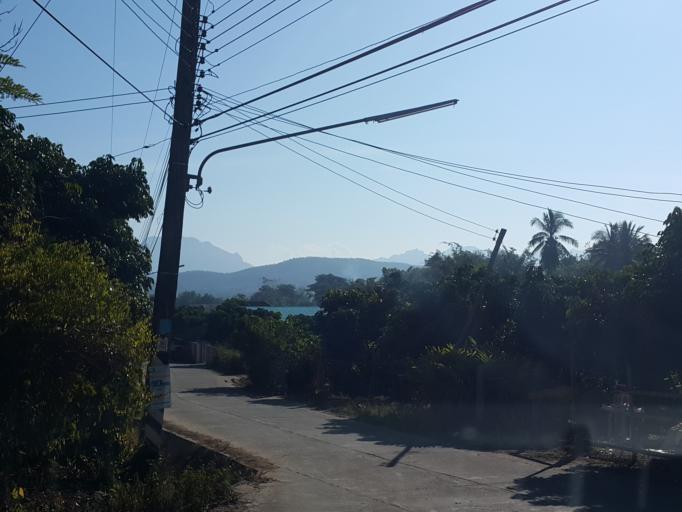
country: TH
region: Chiang Mai
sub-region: Amphoe Chiang Dao
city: Chiang Dao
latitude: 19.4687
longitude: 98.9525
